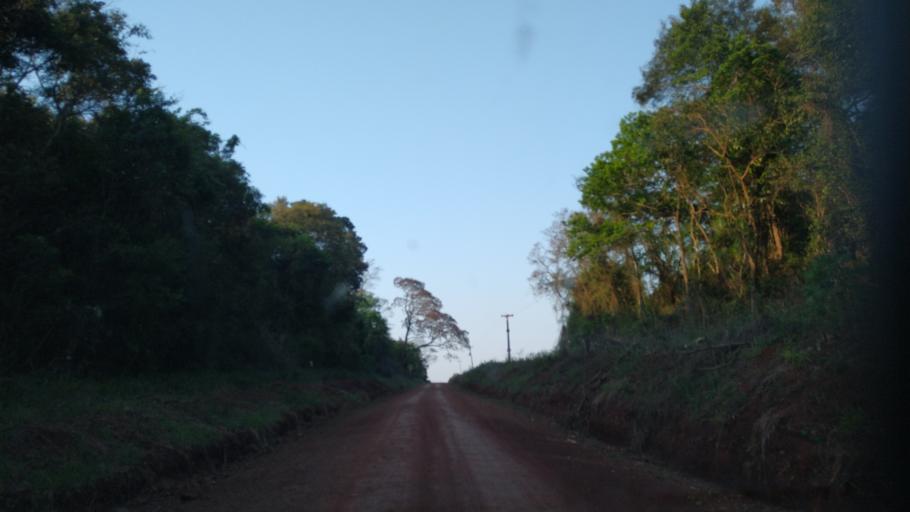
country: AR
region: Misiones
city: Jardin America
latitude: -27.0826
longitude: -55.2745
